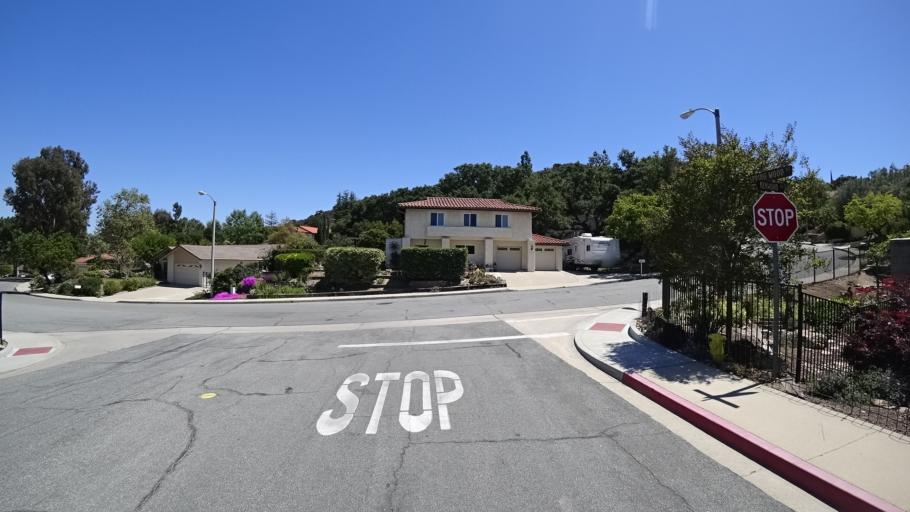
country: US
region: California
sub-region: Ventura County
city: Casa Conejo
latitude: 34.1750
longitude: -118.8950
